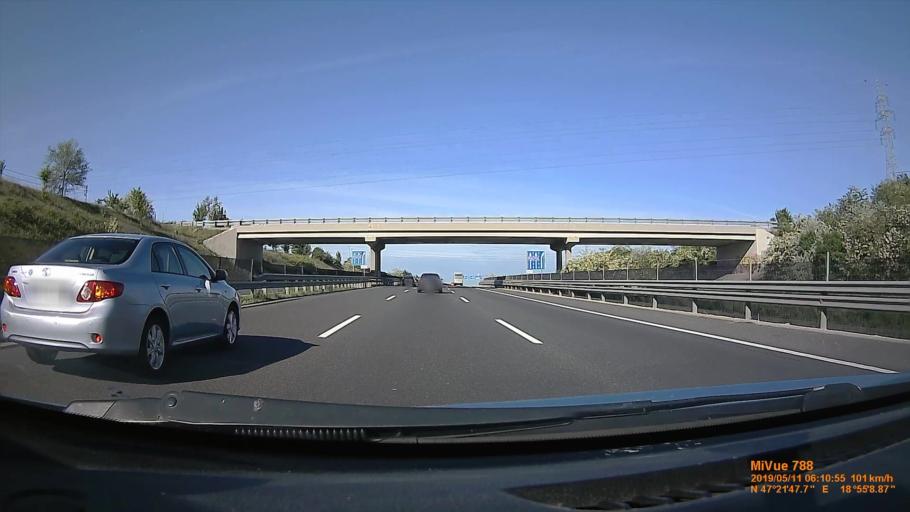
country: HU
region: Pest
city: Erd
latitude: 47.3623
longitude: 18.9188
